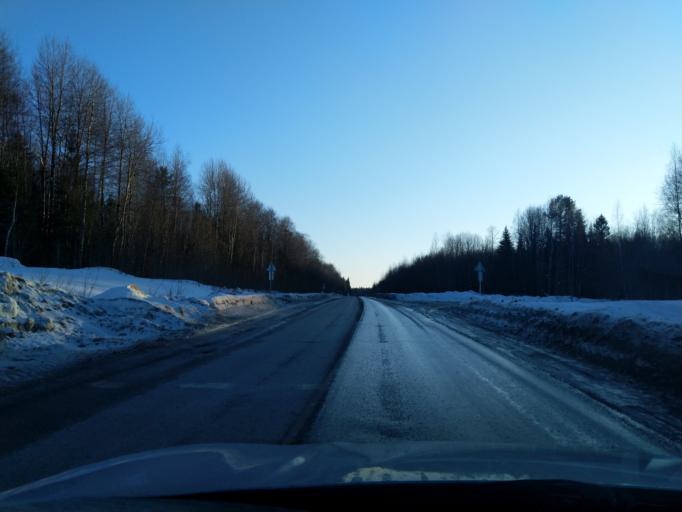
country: RU
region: Perm
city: Dobryanka
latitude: 58.4524
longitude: 56.5465
